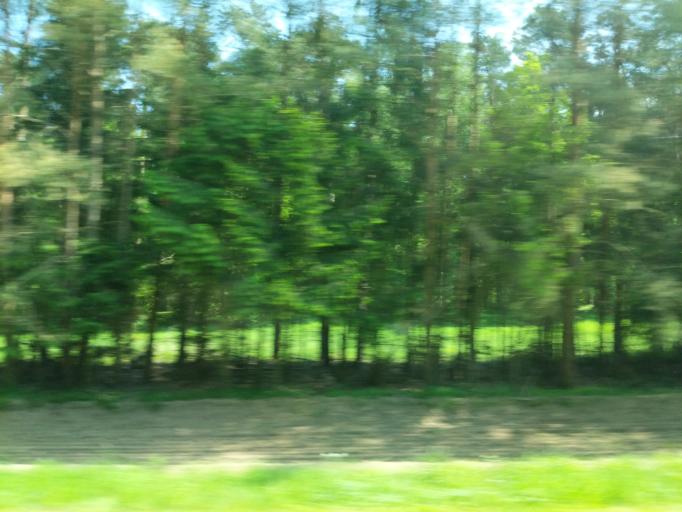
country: DE
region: Mecklenburg-Vorpommern
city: Stralendorf
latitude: 53.5201
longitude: 11.3003
